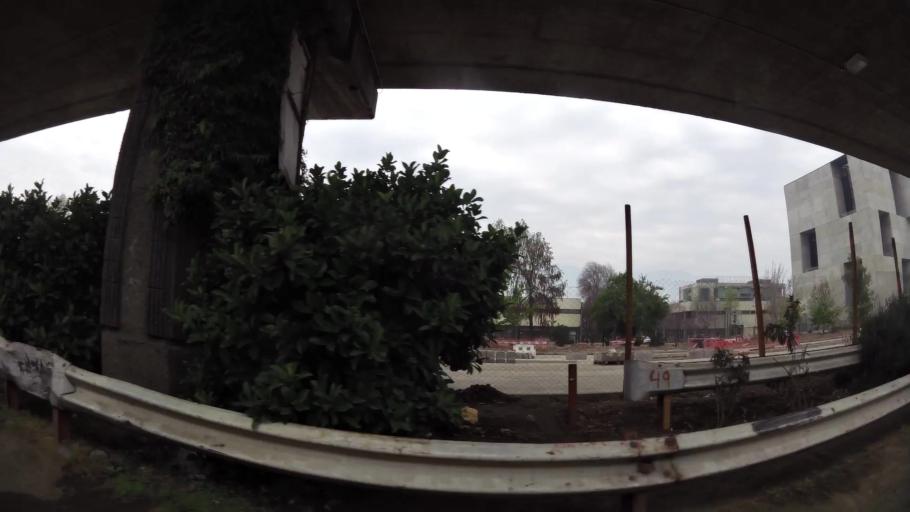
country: CL
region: Santiago Metropolitan
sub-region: Provincia de Santiago
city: Villa Presidente Frei, Nunoa, Santiago, Chile
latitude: -33.4969
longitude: -70.6163
